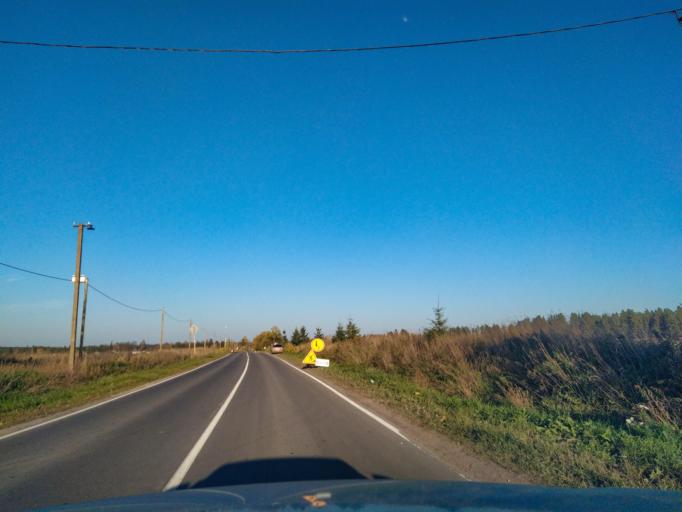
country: RU
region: Leningrad
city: Siverskiy
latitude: 59.3295
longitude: 30.0432
